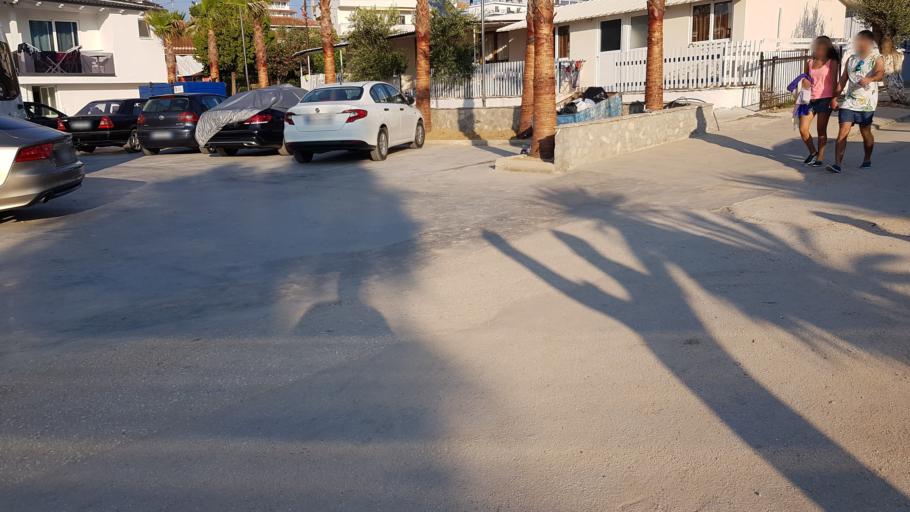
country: AL
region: Vlore
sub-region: Rrethi i Sarandes
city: Xarre
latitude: 39.7724
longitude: 20.0022
